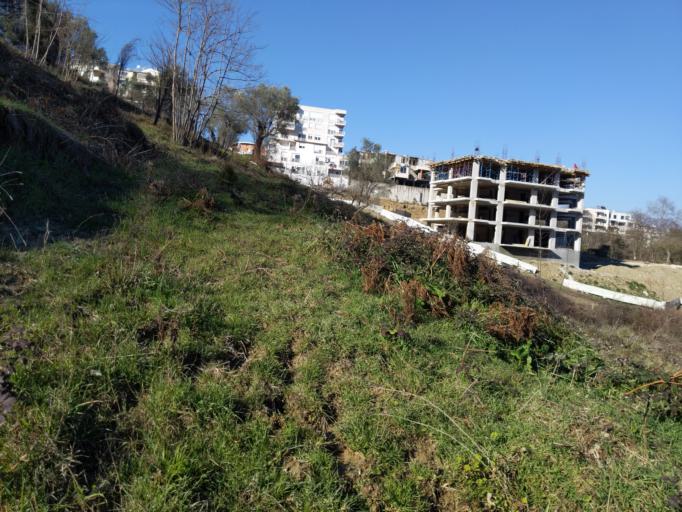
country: AL
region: Tirane
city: Tirana
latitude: 41.3085
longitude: 19.8026
